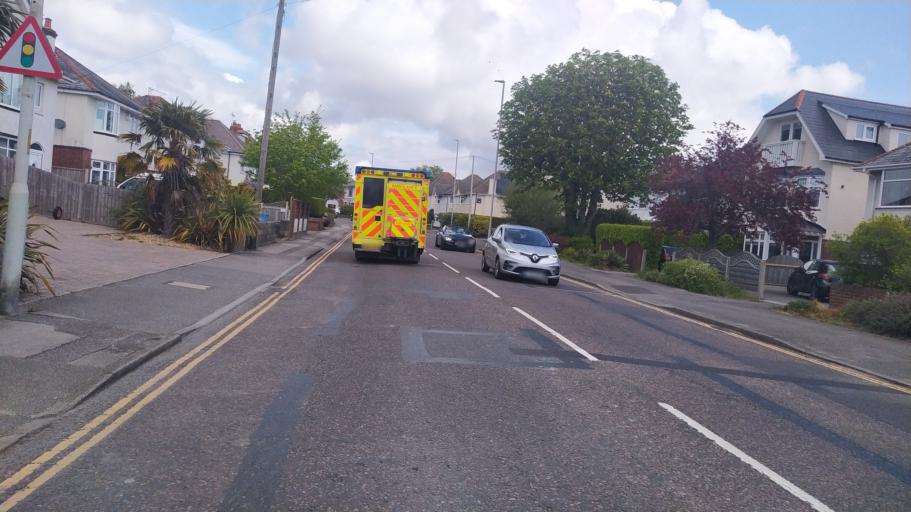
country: GB
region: England
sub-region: Dorset
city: Parkstone
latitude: 50.7175
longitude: -1.9534
